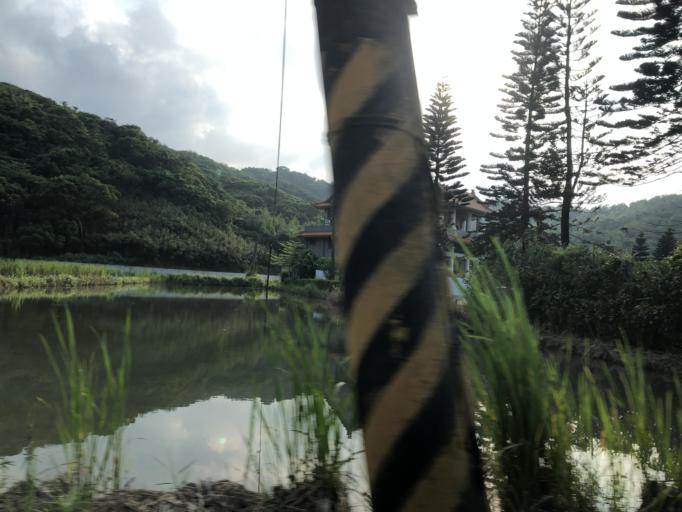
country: TW
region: Taiwan
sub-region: Keelung
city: Keelung
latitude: 25.2055
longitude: 121.6482
